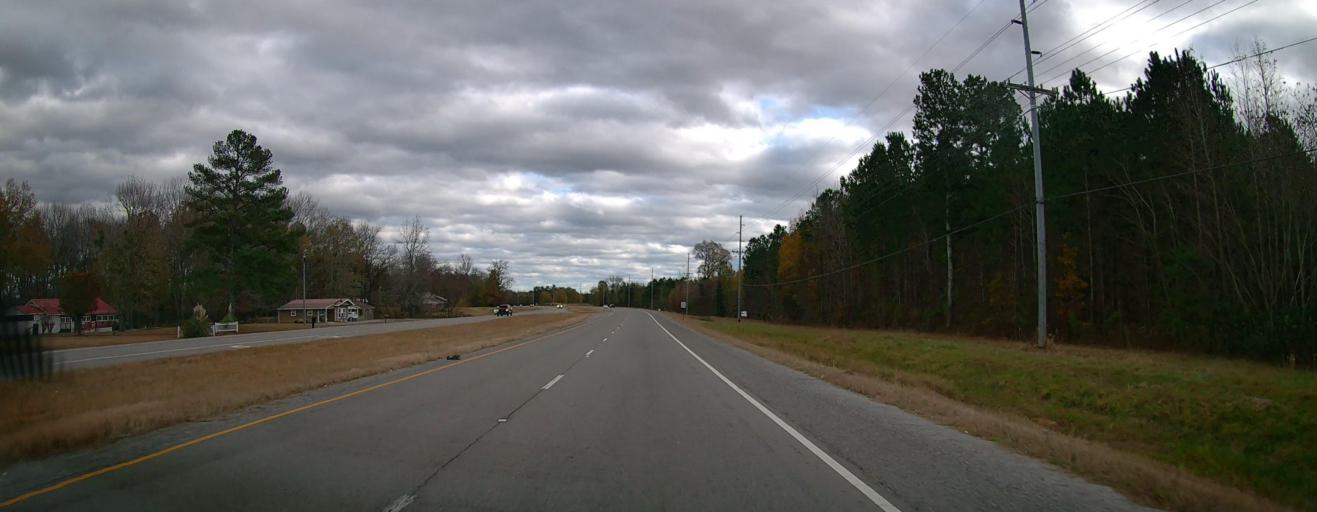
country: US
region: Alabama
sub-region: Lawrence County
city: Town Creek
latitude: 34.5769
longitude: -87.4041
